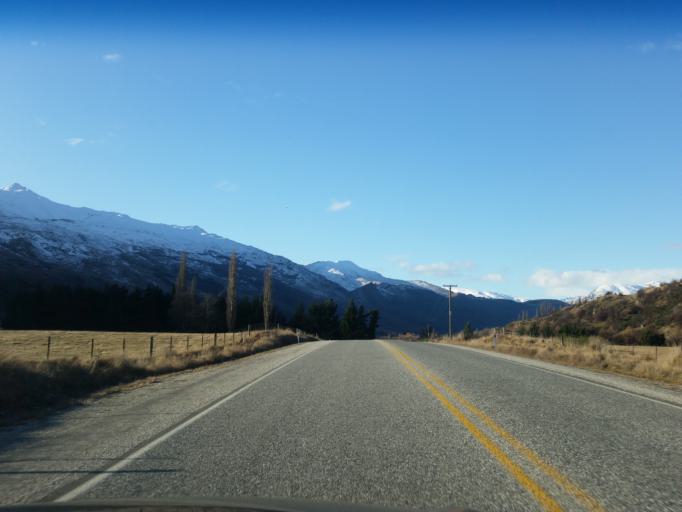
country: NZ
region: Otago
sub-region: Queenstown-Lakes District
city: Queenstown
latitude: -44.9689
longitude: 168.7043
